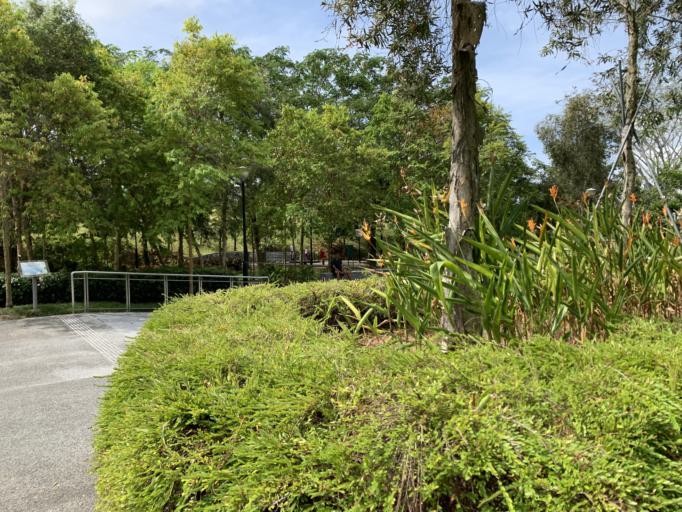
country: MY
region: Johor
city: Johor Bahru
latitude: 1.3692
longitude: 103.7737
